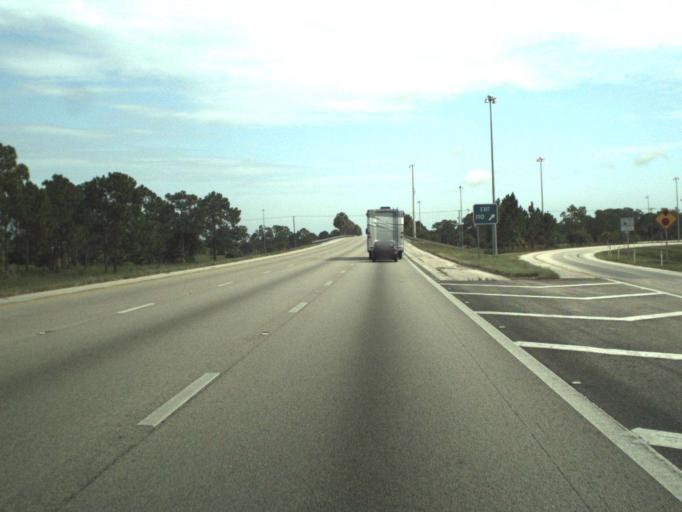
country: US
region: Florida
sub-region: Martin County
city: Palm City
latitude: 27.1576
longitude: -80.3876
